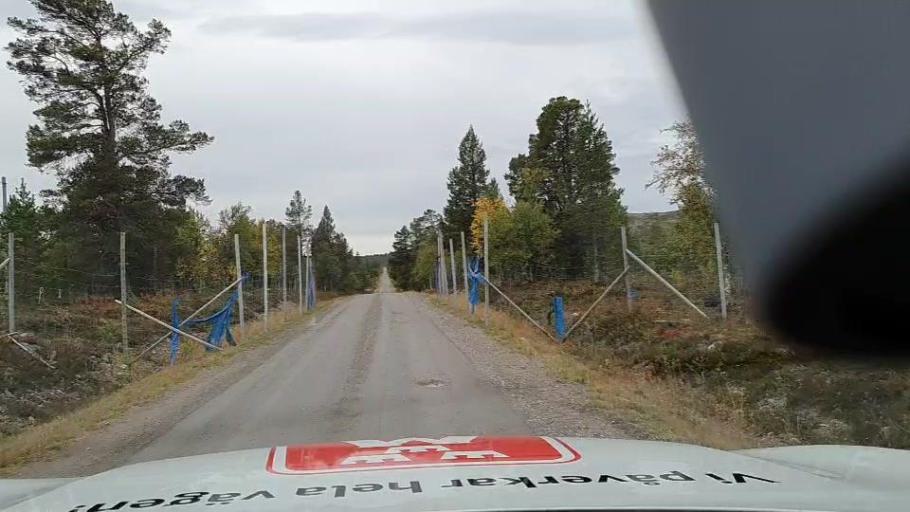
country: NO
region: Hedmark
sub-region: Engerdal
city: Engerdal
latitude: 62.1214
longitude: 12.8672
